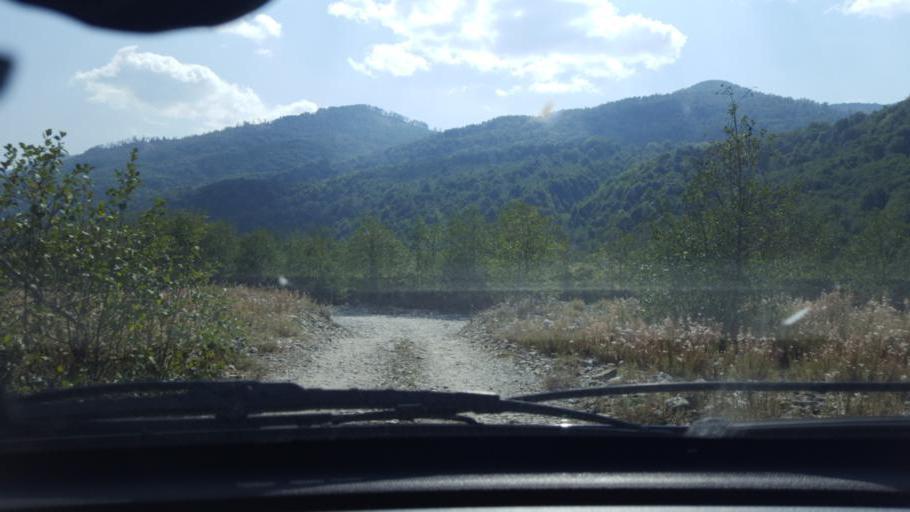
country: ME
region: Andrijevica
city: Andrijevica
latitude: 42.5951
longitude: 19.6746
